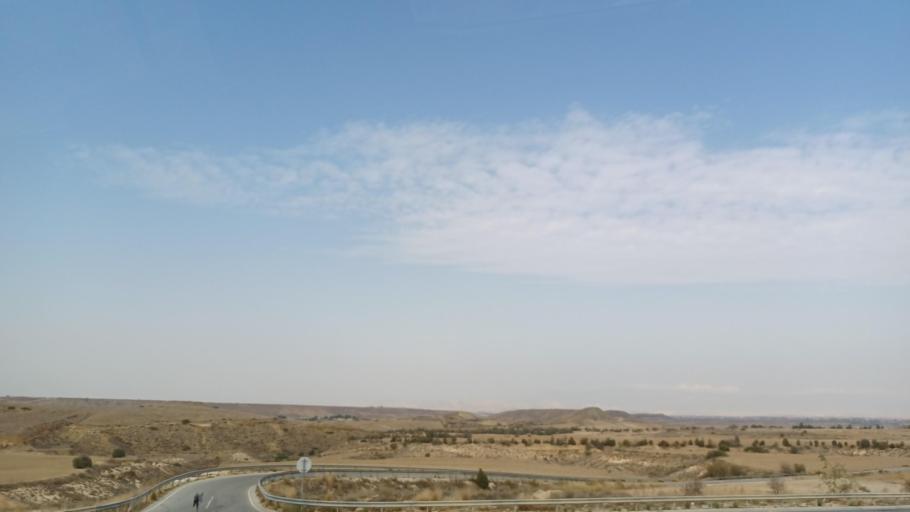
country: CY
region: Lefkosia
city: Meniko
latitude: 35.0689
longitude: 33.1160
